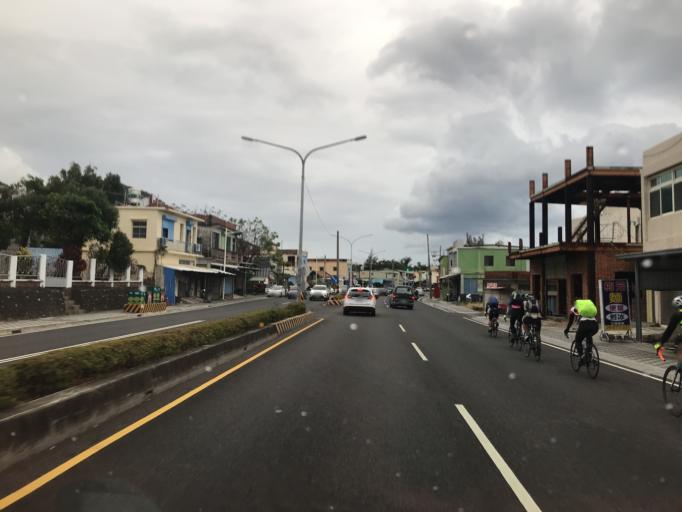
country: TW
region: Taiwan
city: Hengchun
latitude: 22.1906
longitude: 120.6917
